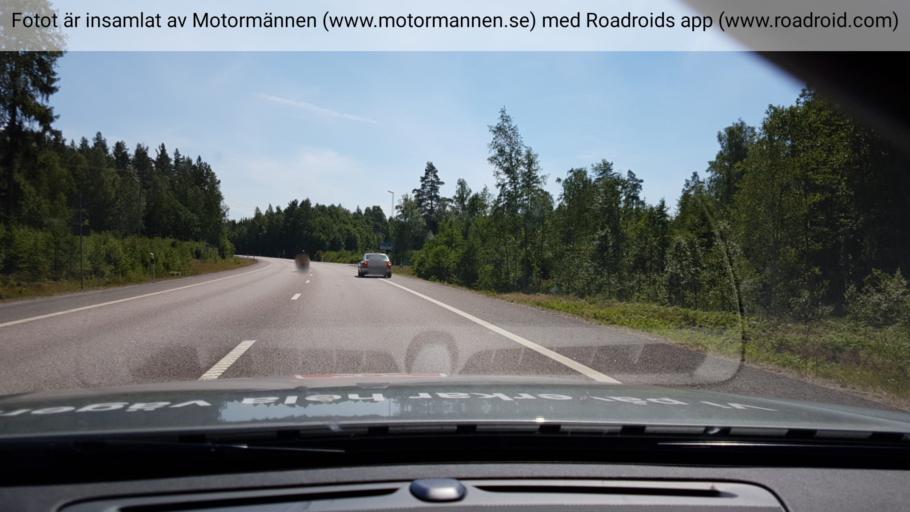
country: SE
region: OErebro
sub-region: Laxa Kommun
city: Laxa
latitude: 58.9539
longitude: 14.6254
